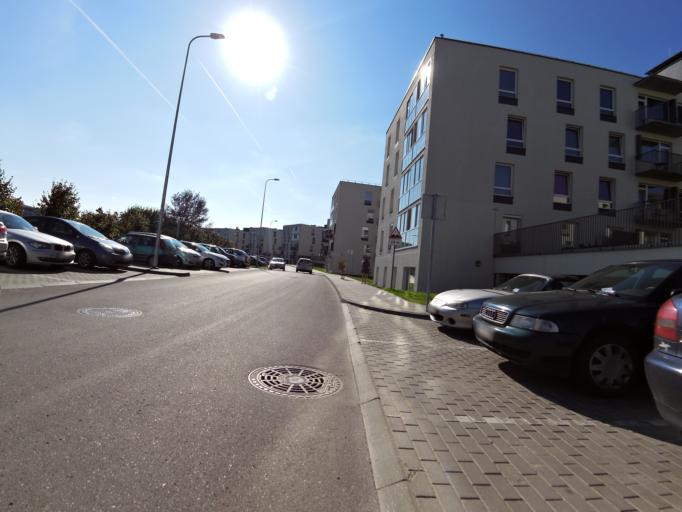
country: LT
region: Vilnius County
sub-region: Vilnius
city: Vilnius
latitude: 54.7192
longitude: 25.2792
